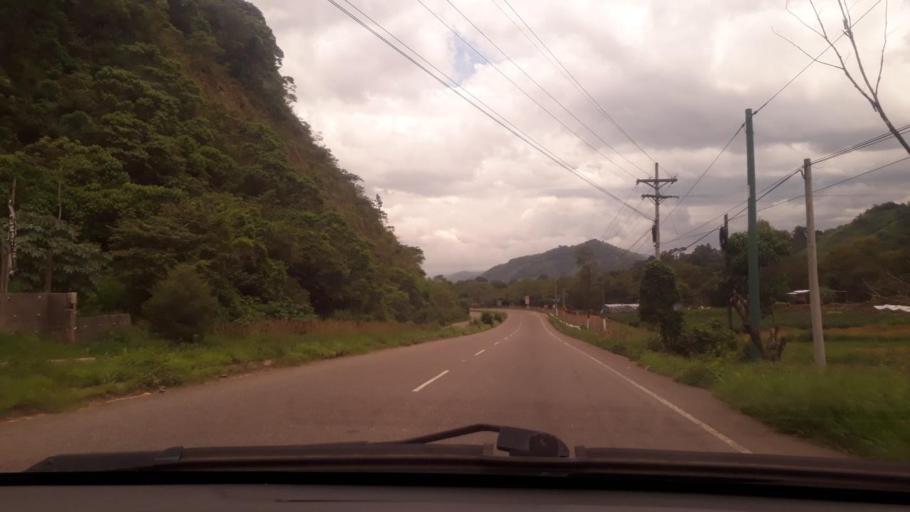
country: GT
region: Santa Rosa
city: Oratorio
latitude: 14.2562
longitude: -90.2127
